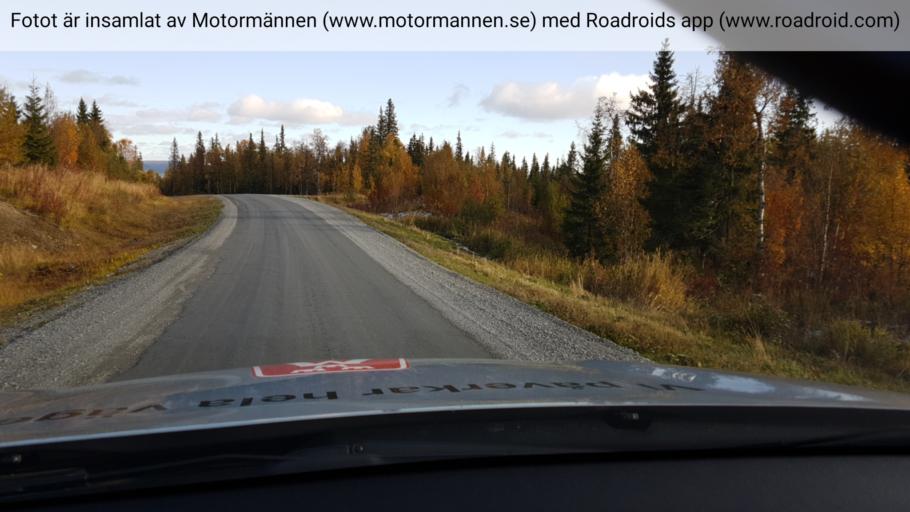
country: SE
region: Vaesterbotten
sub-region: Vilhelmina Kommun
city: Sjoberg
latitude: 64.7715
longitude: 15.9439
